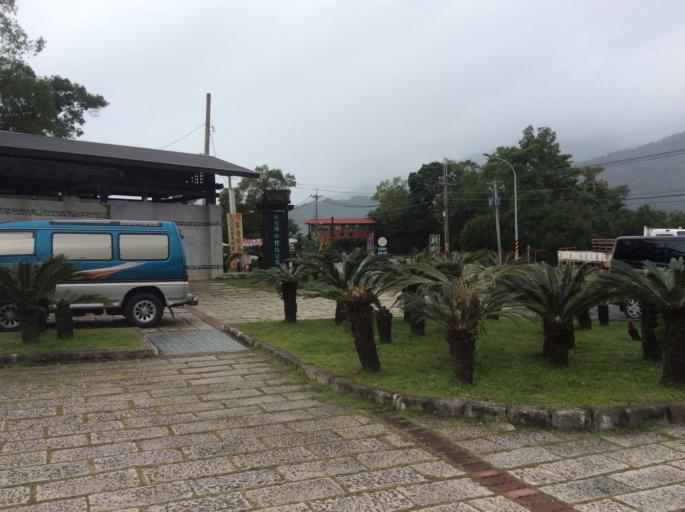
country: TW
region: Taiwan
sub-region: Hualien
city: Hualian
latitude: 23.4657
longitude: 121.3573
